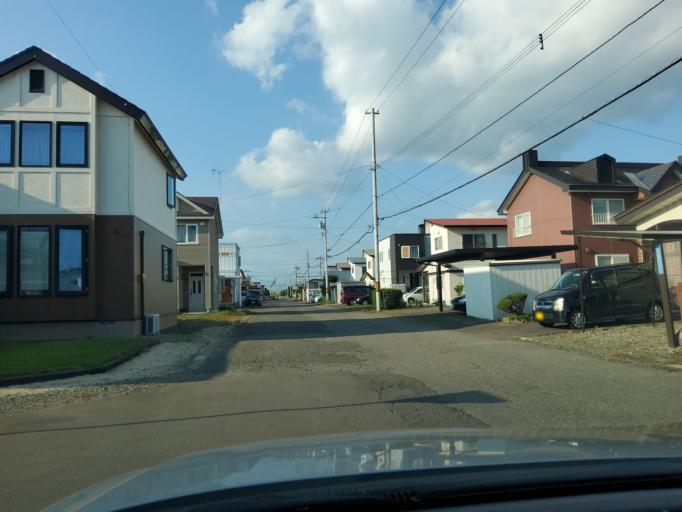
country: JP
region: Hokkaido
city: Obihiro
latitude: 42.9103
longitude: 143.1625
